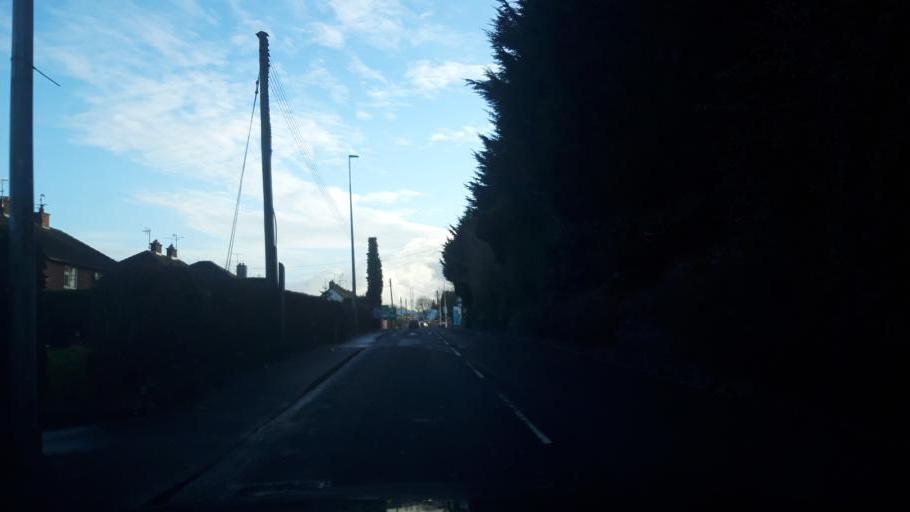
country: GB
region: Northern Ireland
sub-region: Dungannon District
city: Dungannon
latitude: 54.5108
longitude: -6.7681
